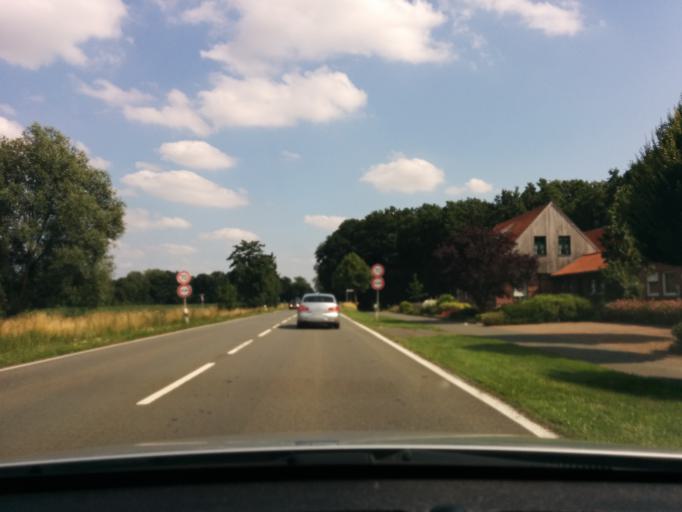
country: DE
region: North Rhine-Westphalia
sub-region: Regierungsbezirk Munster
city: Ochtrup
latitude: 52.1935
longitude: 7.2488
